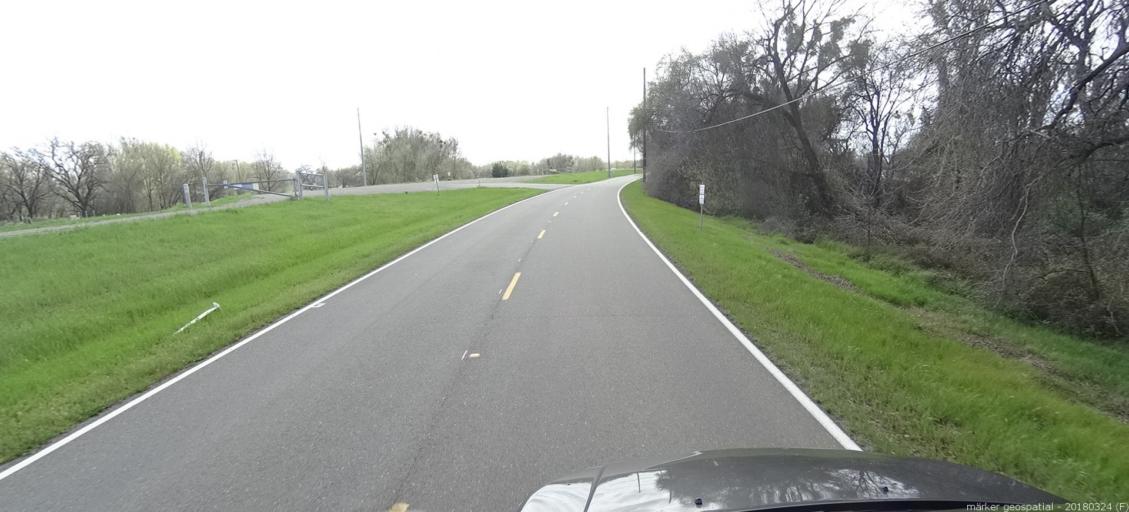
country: US
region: California
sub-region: Yolo County
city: West Sacramento
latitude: 38.7045
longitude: -121.6181
